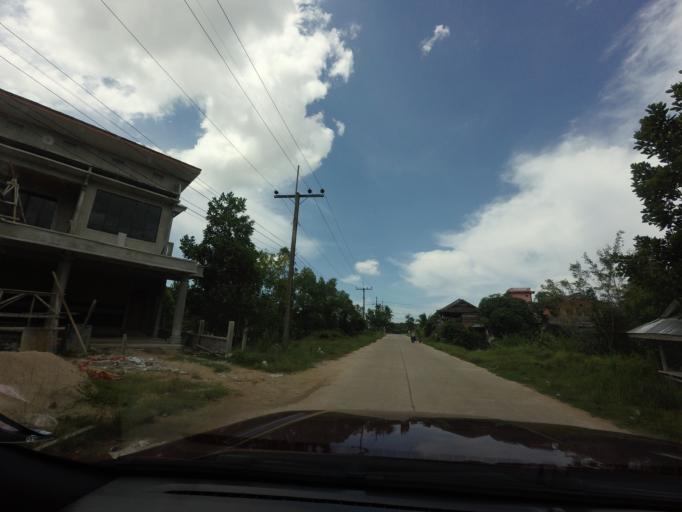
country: TH
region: Narathiwat
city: Bacho
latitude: 6.4883
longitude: 101.6653
